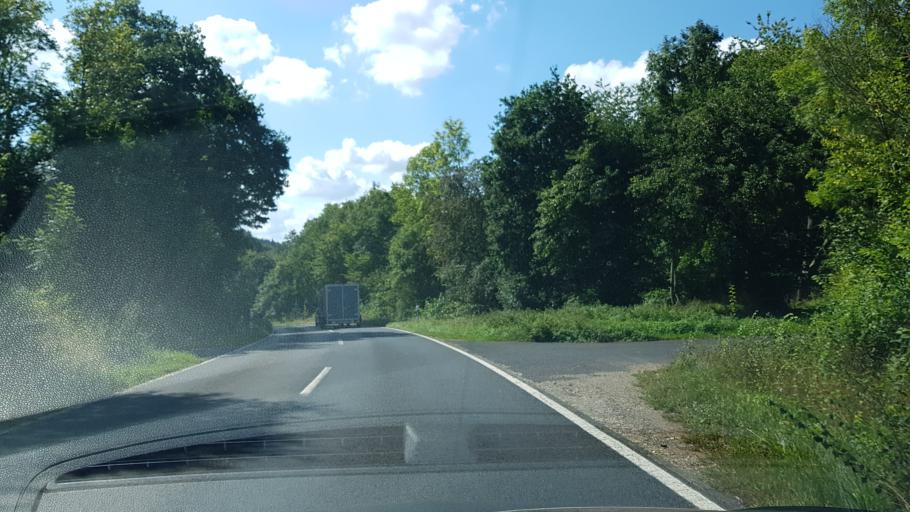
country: DE
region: Rheinland-Pfalz
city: Ernst
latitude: 50.1480
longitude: 7.2573
